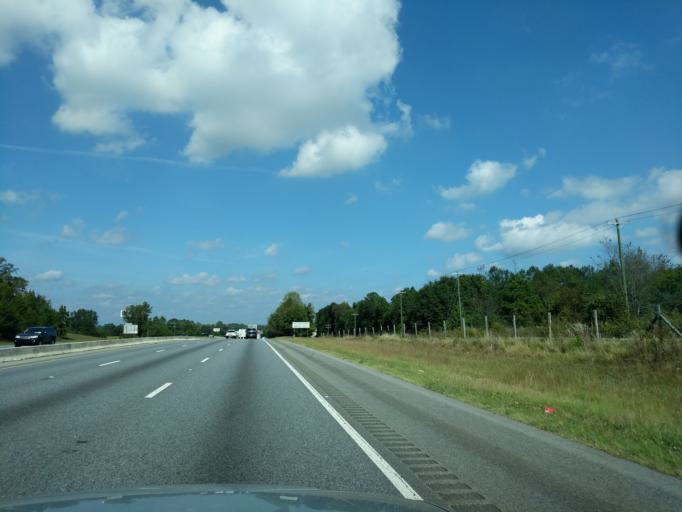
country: US
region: South Carolina
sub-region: Anderson County
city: Piedmont
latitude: 34.7115
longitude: -82.4989
